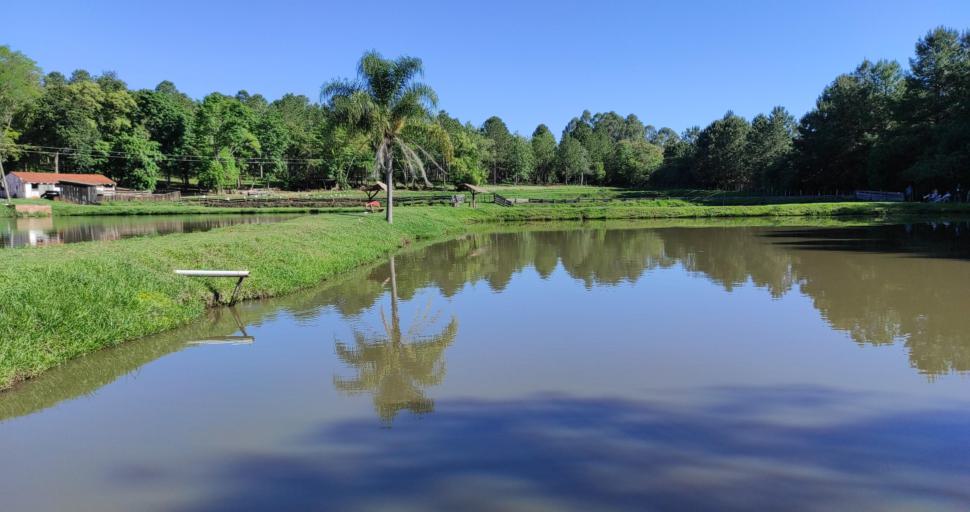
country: AR
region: Misiones
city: Ruiz de Montoya
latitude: -26.9489
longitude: -55.0078
